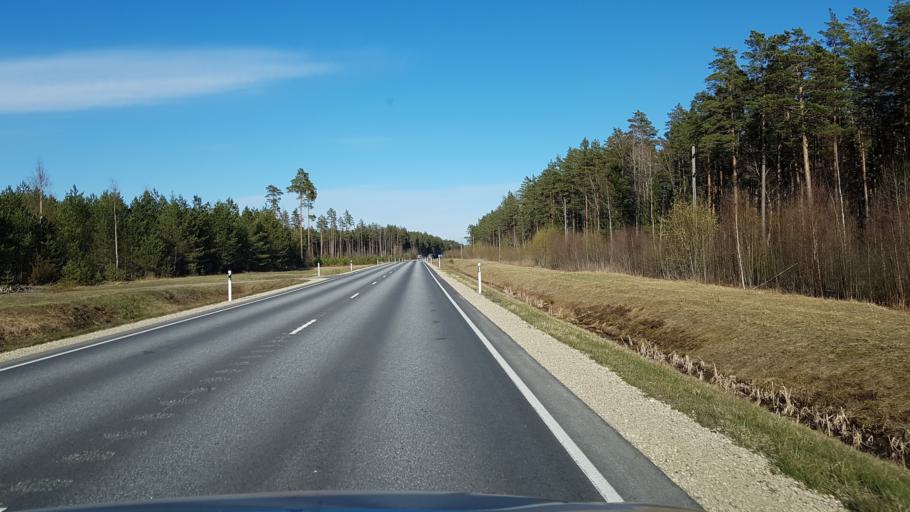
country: EE
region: Jogevamaa
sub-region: Mustvee linn
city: Mustvee
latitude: 58.9745
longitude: 27.1316
